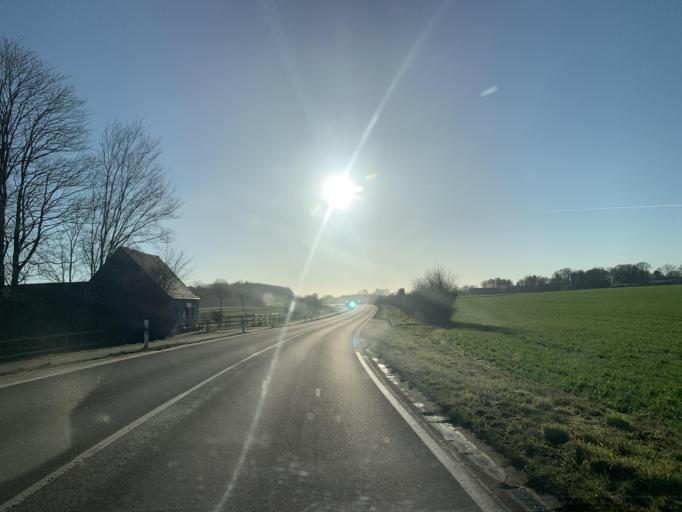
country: DE
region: North Rhine-Westphalia
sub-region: Regierungsbezirk Munster
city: Dulmen
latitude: 51.8669
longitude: 7.2871
